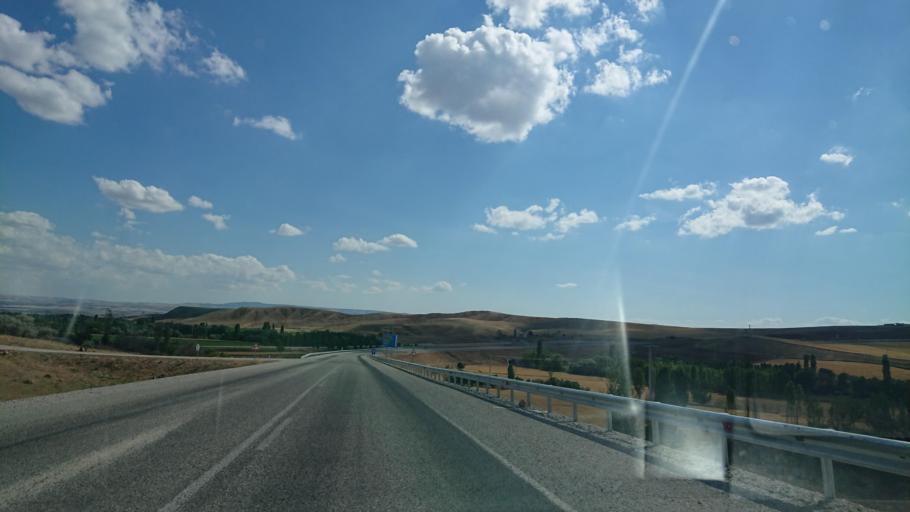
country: TR
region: Ankara
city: Evren
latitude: 39.1050
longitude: 33.9119
